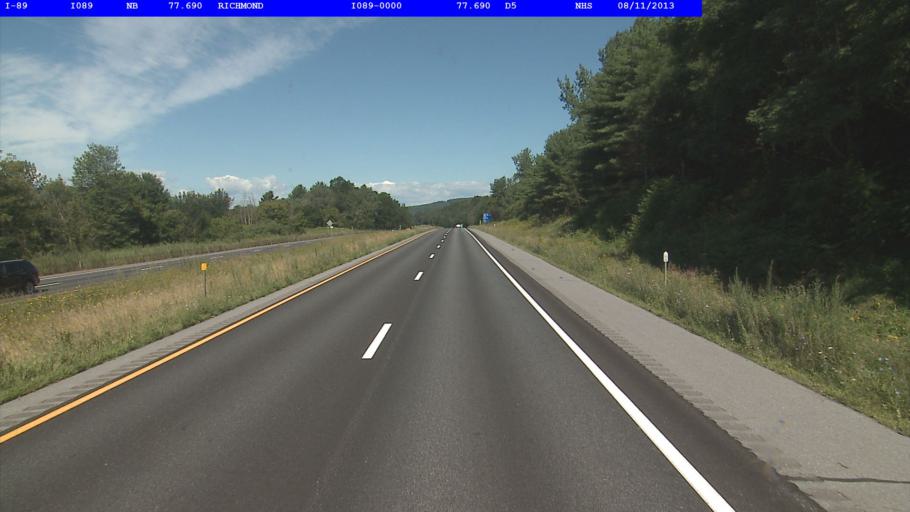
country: US
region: Vermont
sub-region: Chittenden County
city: Williston
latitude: 44.4187
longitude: -72.9987
